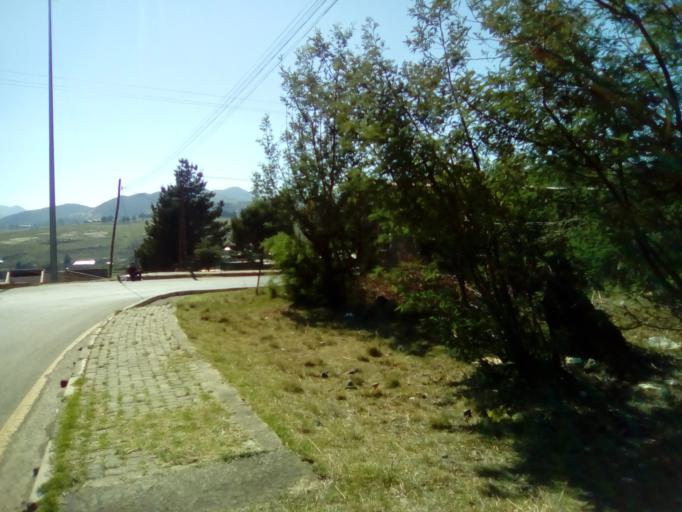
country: LS
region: Qacha's Nek
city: Qacha's Nek
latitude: -30.1086
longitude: 28.6829
